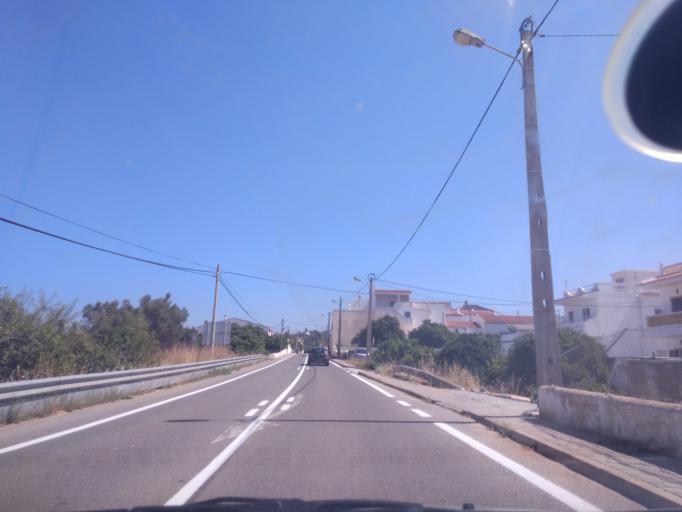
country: PT
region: Faro
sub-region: Lagos
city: Lagos
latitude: 37.1252
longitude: -8.6953
